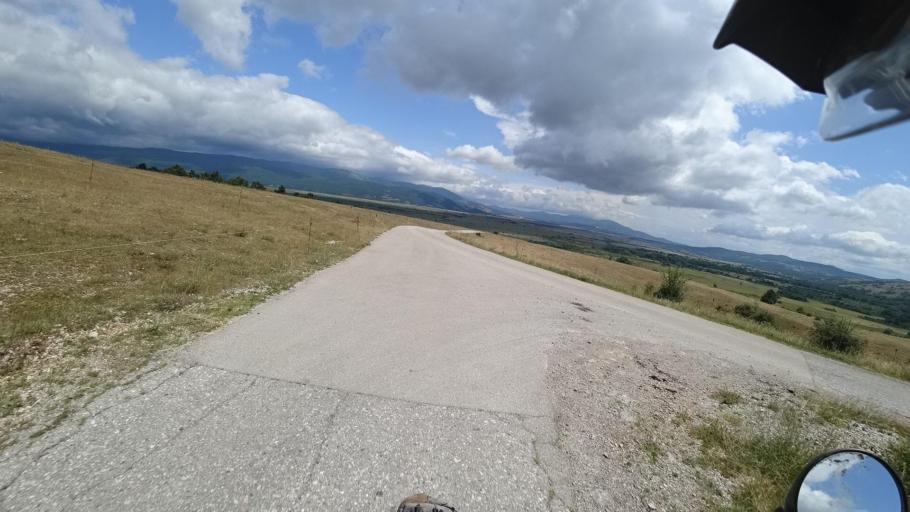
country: HR
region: Licko-Senjska
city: Jezerce
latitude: 44.6155
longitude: 15.6580
